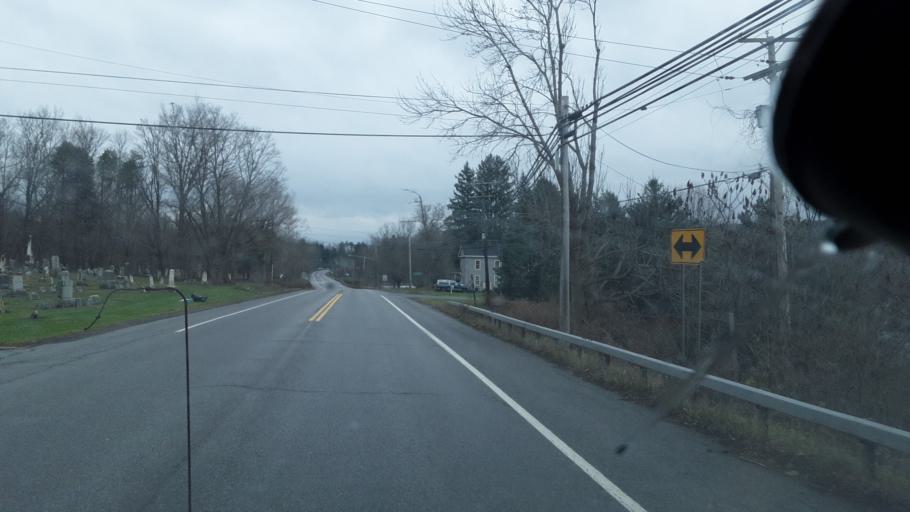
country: US
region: New York
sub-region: Erie County
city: Holland
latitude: 42.7044
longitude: -78.5749
